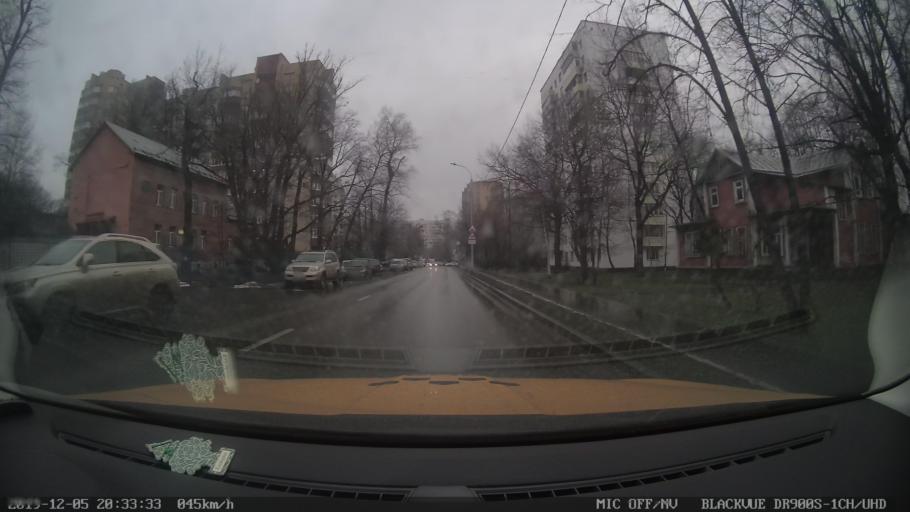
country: RU
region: Moscow
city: Likhobory
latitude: 55.8225
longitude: 37.5699
